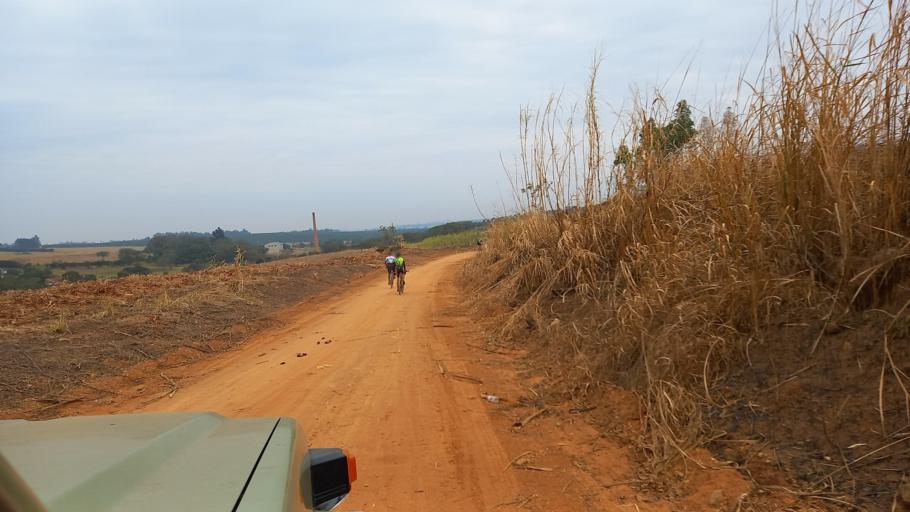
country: BR
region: Sao Paulo
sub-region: Moji-Guacu
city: Mogi-Gaucu
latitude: -22.2716
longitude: -46.8411
